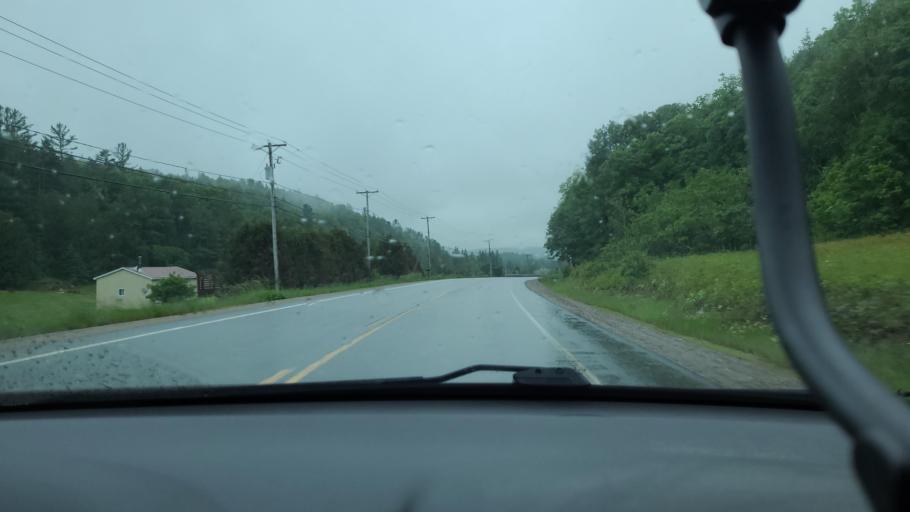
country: CA
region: Quebec
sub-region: Outaouais
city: Saint-Andre-Avellin
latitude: 45.8558
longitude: -75.0483
